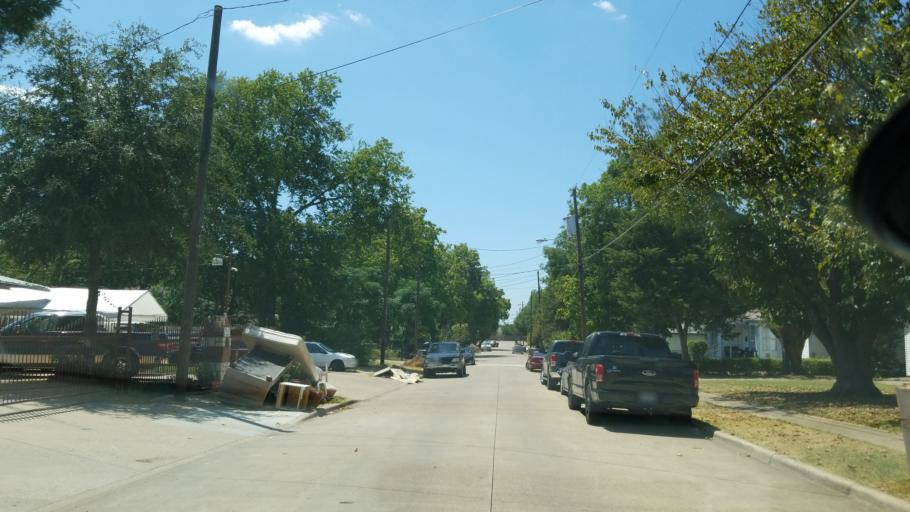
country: US
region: Texas
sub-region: Dallas County
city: Cockrell Hill
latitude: 32.7274
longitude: -96.8888
